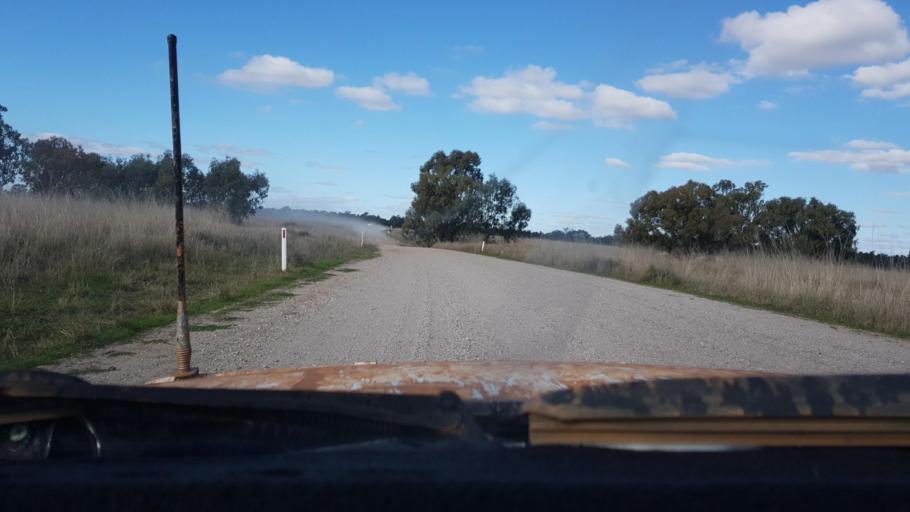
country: AU
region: New South Wales
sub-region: Lachlan
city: Condobolin
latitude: -33.1362
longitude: 147.2737
